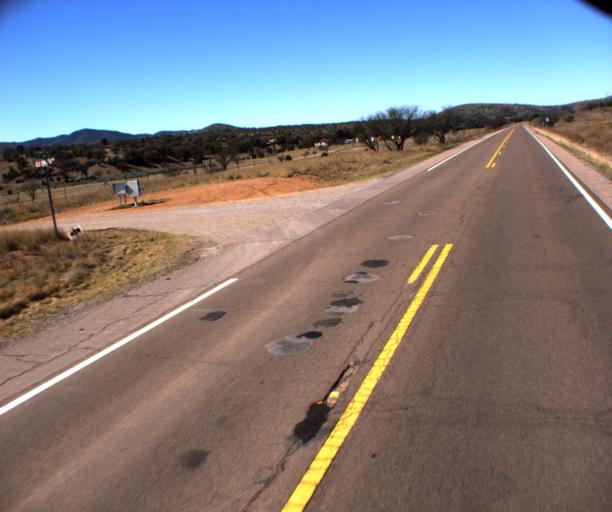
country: US
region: Arizona
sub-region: Pima County
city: Corona de Tucson
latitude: 31.6702
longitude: -110.6738
